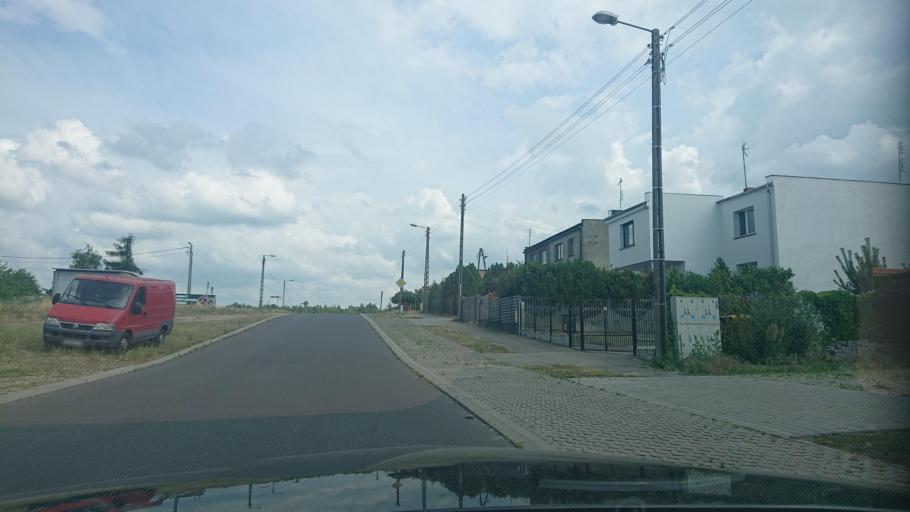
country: PL
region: Greater Poland Voivodeship
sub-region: Powiat gnieznienski
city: Gniezno
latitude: 52.5038
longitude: 17.5905
